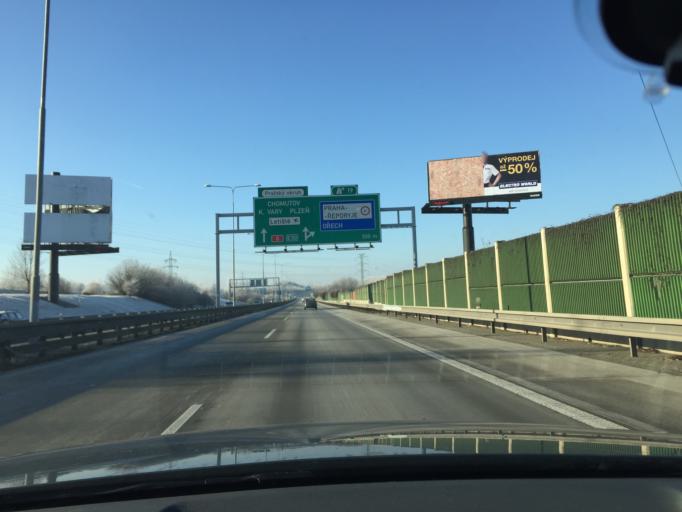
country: CZ
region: Central Bohemia
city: Trebotov
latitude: 50.0245
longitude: 14.3089
